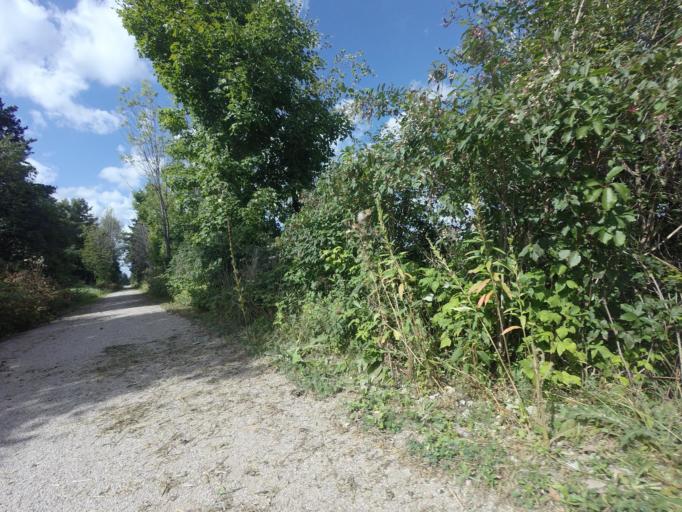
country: CA
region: Ontario
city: Huron East
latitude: 43.7283
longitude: -81.4120
